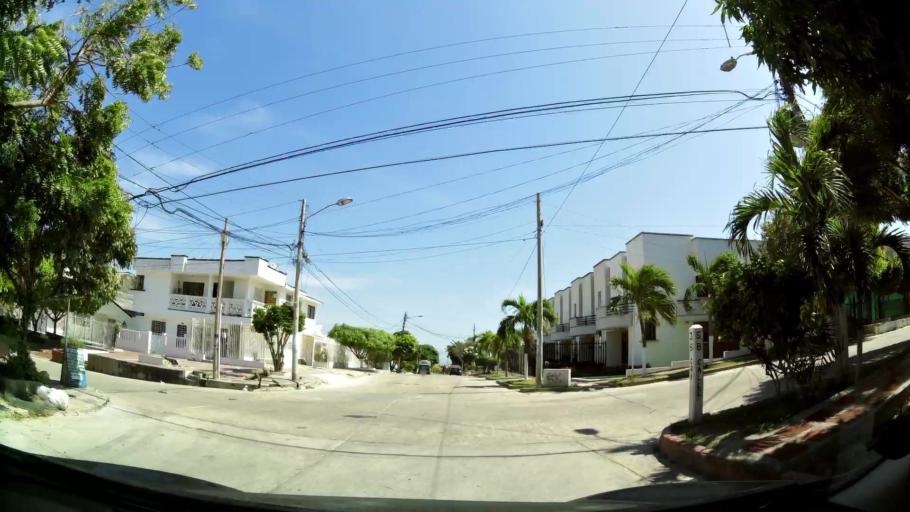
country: CO
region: Atlantico
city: Barranquilla
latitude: 10.9805
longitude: -74.7987
